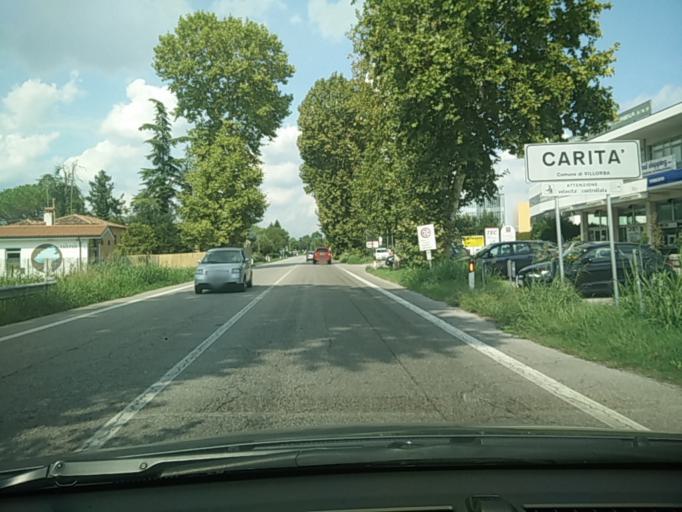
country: IT
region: Veneto
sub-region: Provincia di Treviso
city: Lancenigo-Villorba
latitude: 45.7044
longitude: 12.2596
